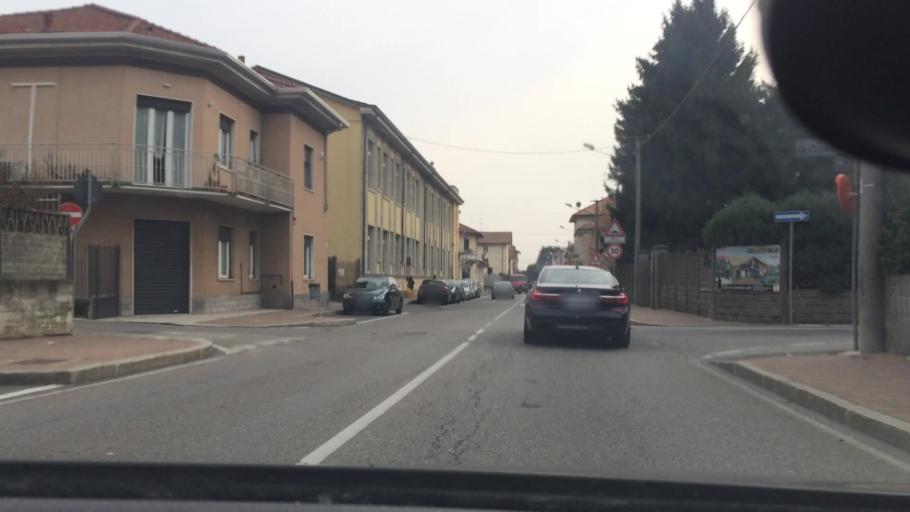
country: IT
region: Lombardy
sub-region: Provincia di Monza e Brianza
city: Cogliate
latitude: 45.6453
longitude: 9.0793
